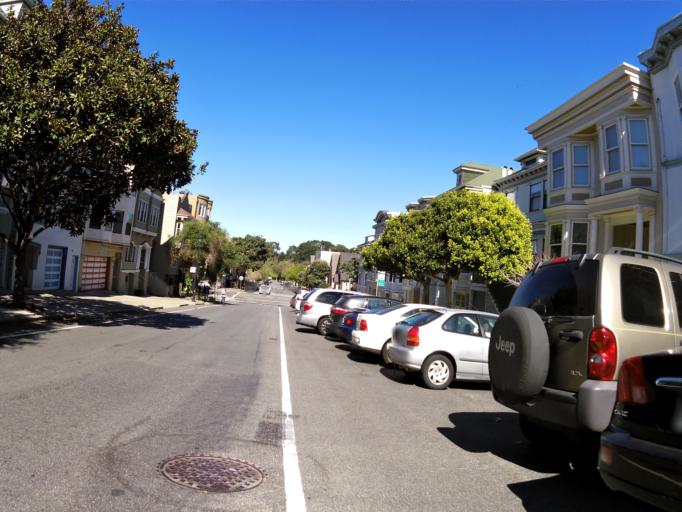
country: US
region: California
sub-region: San Francisco County
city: San Francisco
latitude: 37.7636
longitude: -122.4620
